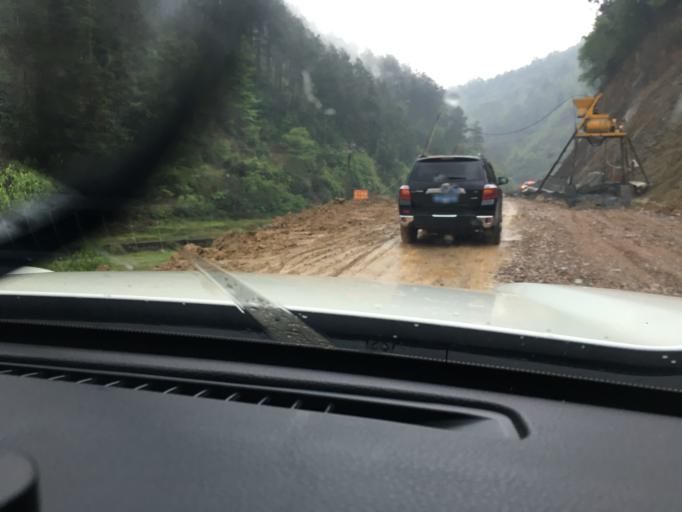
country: CN
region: Guizhou Sheng
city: Fuxing
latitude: 28.0735
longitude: 107.9060
